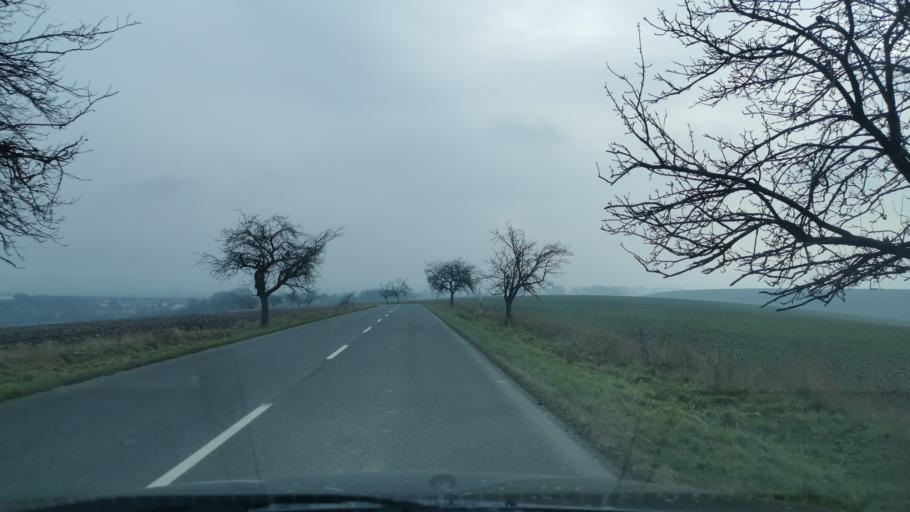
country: SK
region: Trnavsky
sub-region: Okres Senica
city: Senica
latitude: 48.7142
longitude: 17.3274
